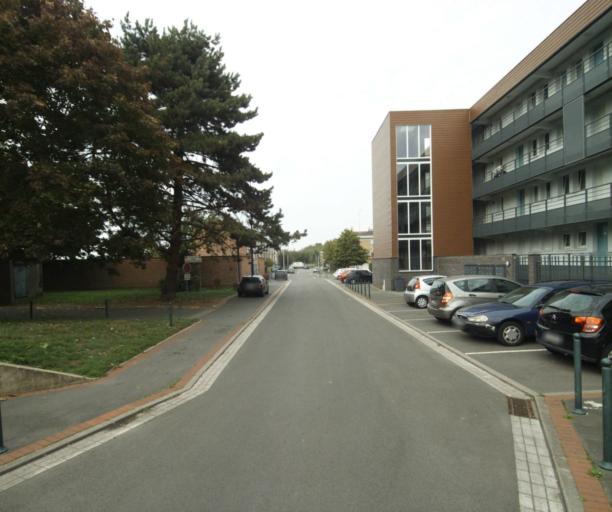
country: FR
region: Nord-Pas-de-Calais
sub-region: Departement du Nord
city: Loos
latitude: 50.6097
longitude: 3.0054
